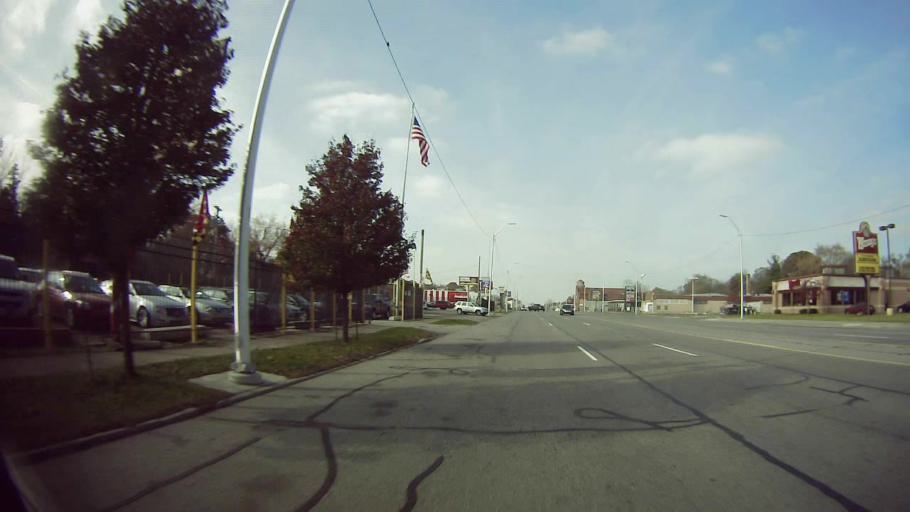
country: US
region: Michigan
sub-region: Wayne County
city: Redford
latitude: 42.4174
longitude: -83.2602
